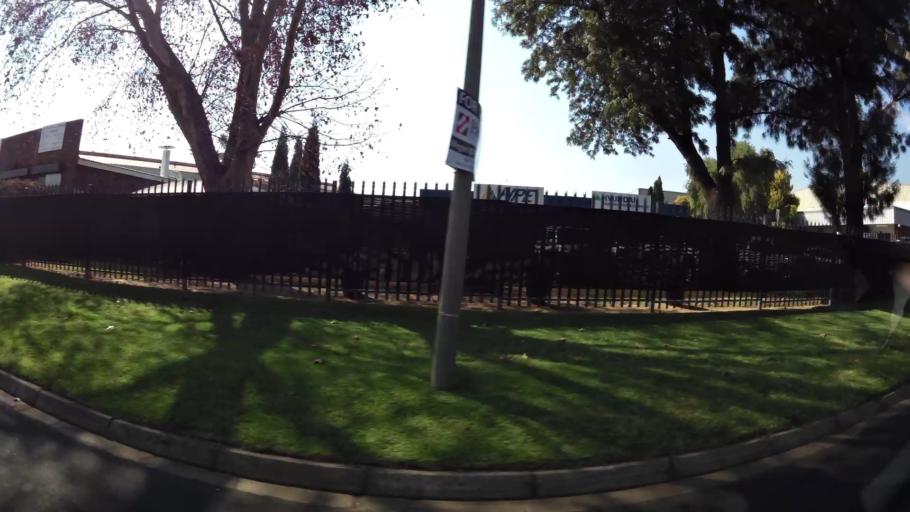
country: ZA
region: Gauteng
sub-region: Ekurhuleni Metropolitan Municipality
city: Boksburg
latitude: -26.1584
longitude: 28.2235
